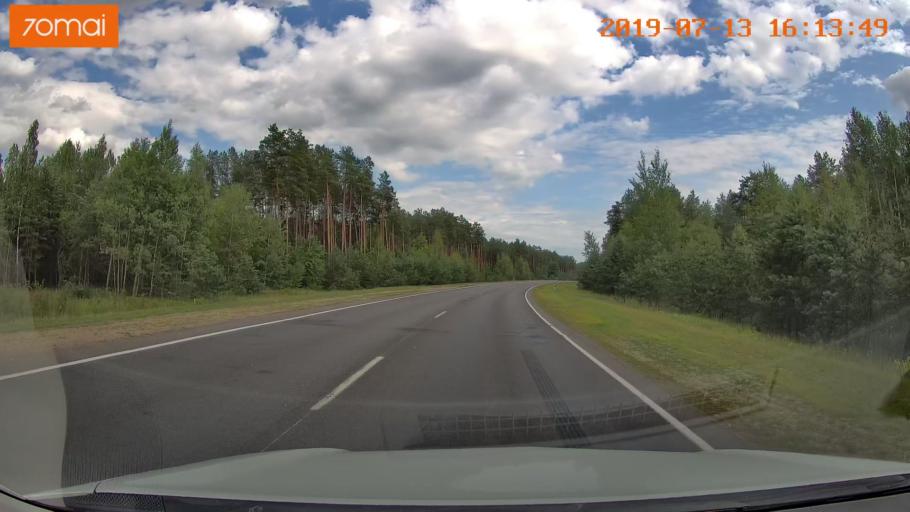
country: BY
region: Mogilev
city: Babruysk
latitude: 53.1605
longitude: 29.3116
